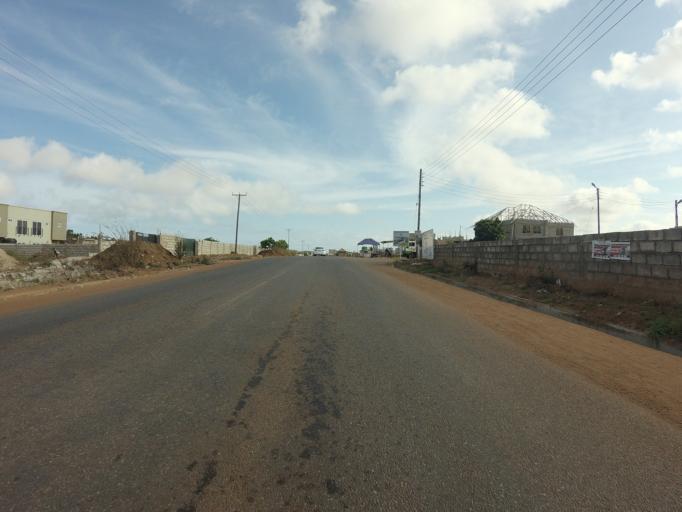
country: GH
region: Greater Accra
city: Teshi Old Town
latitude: 5.5951
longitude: -0.1363
